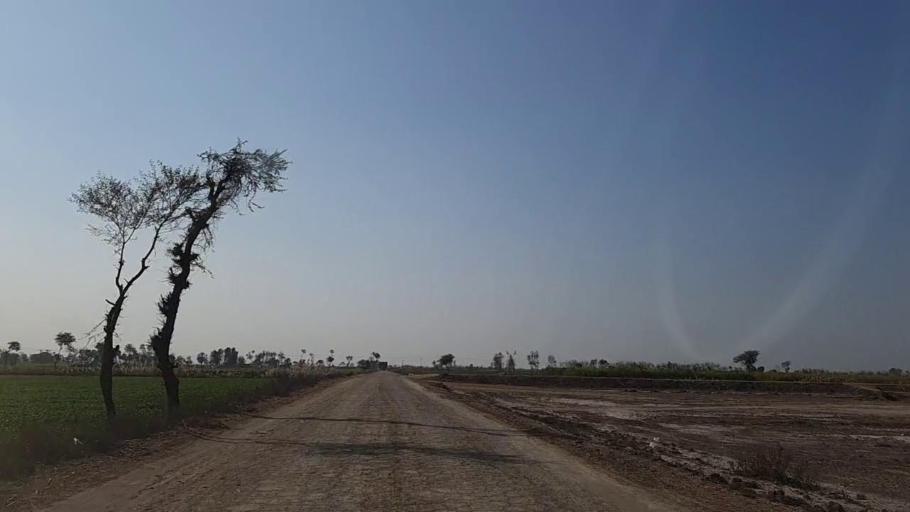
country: PK
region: Sindh
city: Daur
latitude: 26.4711
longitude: 68.3027
